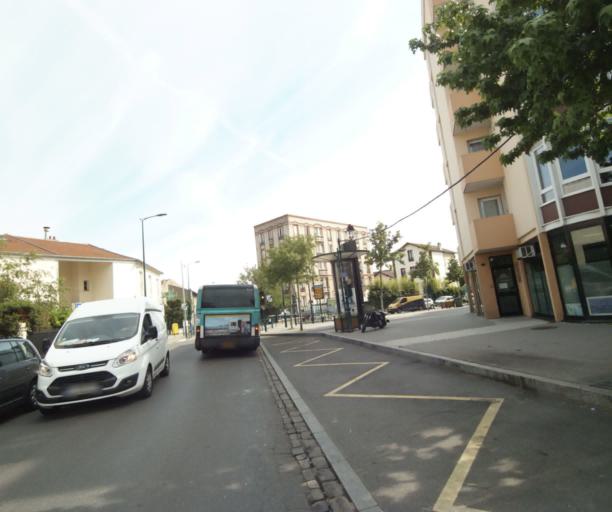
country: FR
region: Ile-de-France
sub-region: Departement des Hauts-de-Seine
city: Colombes
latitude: 48.9149
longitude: 2.2464
